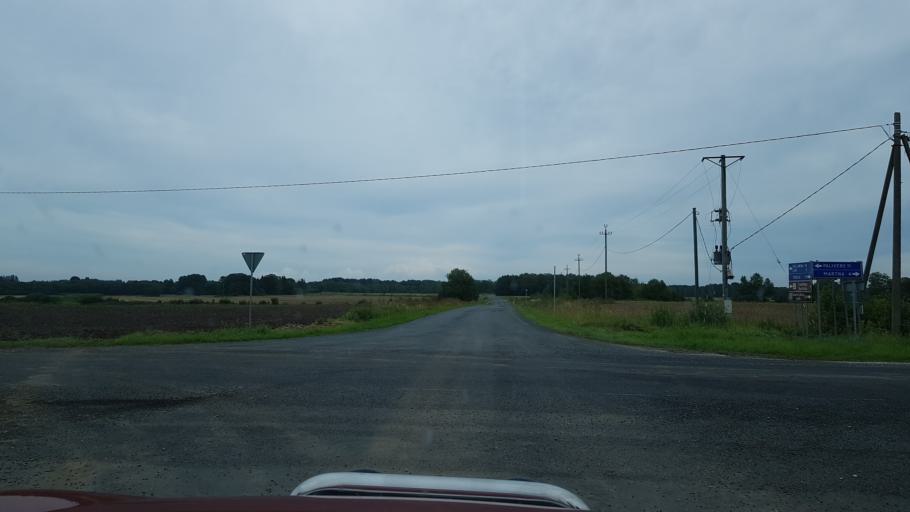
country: EE
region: Laeaene
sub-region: Lihula vald
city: Lihula
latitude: 58.8790
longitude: 23.8530
